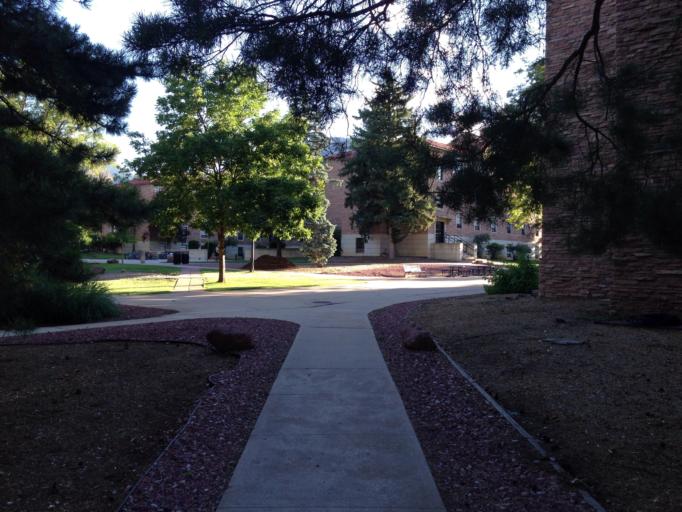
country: US
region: Colorado
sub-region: Boulder County
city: Boulder
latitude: 40.0058
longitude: -105.2654
